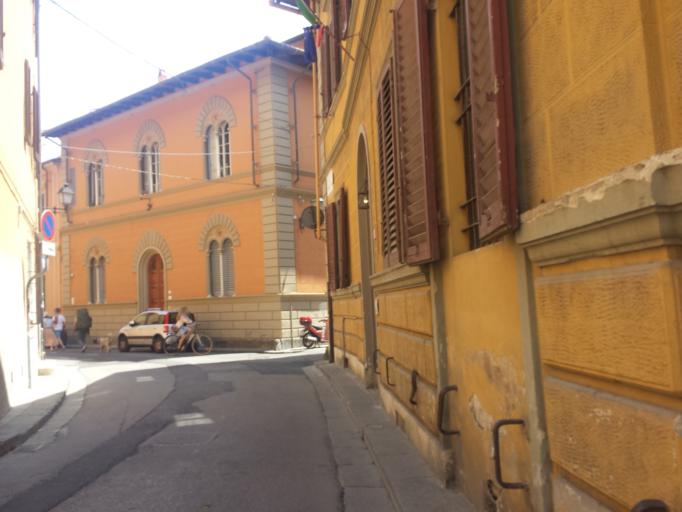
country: IT
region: Tuscany
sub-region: Province of Pisa
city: Pisa
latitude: 43.7215
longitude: 10.4001
